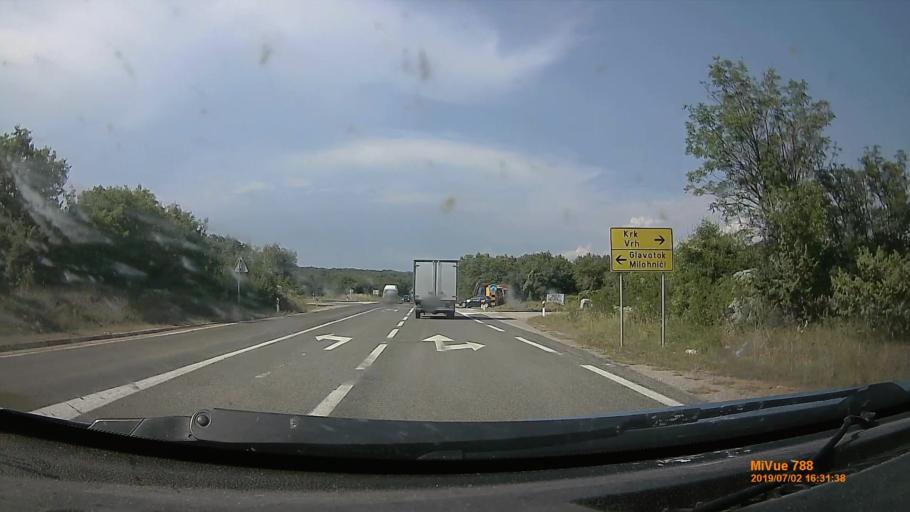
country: HR
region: Primorsko-Goranska
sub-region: Grad Krk
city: Krk
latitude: 45.0559
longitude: 14.4873
